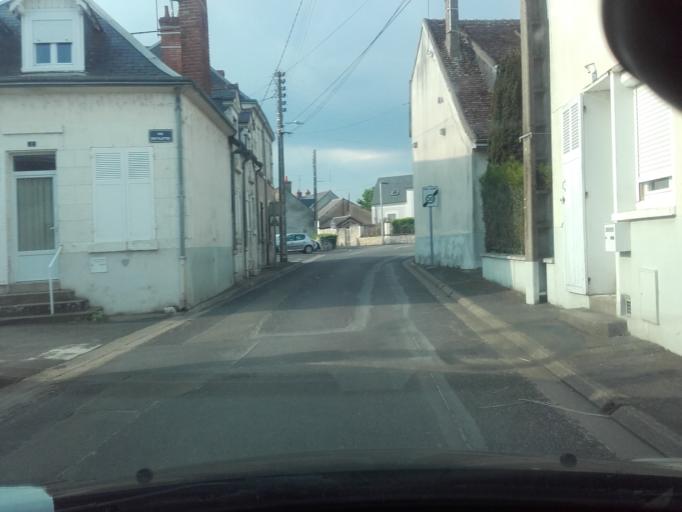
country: FR
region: Centre
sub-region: Departement du Loir-et-Cher
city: Chouzy-sur-Cisse
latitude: 47.5234
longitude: 1.2451
